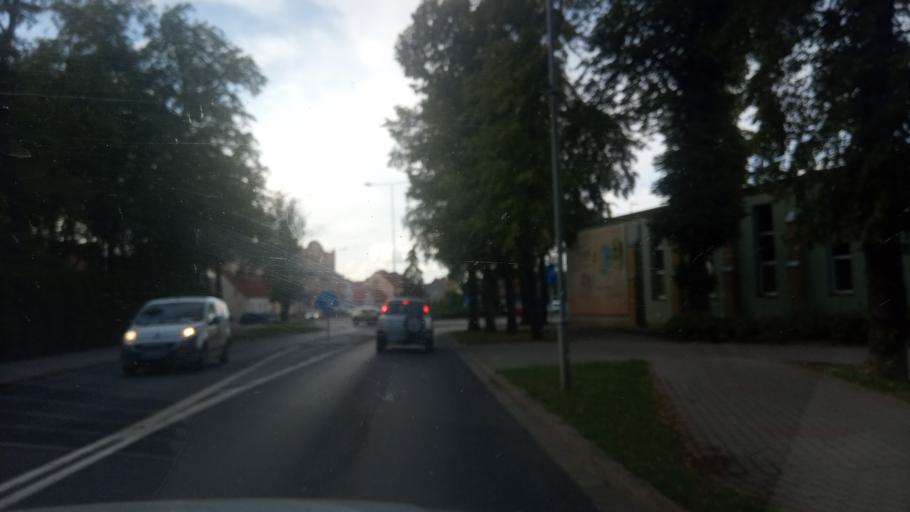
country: PL
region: Greater Poland Voivodeship
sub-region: Powiat zlotowski
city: Zlotow
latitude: 53.3583
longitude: 17.0358
